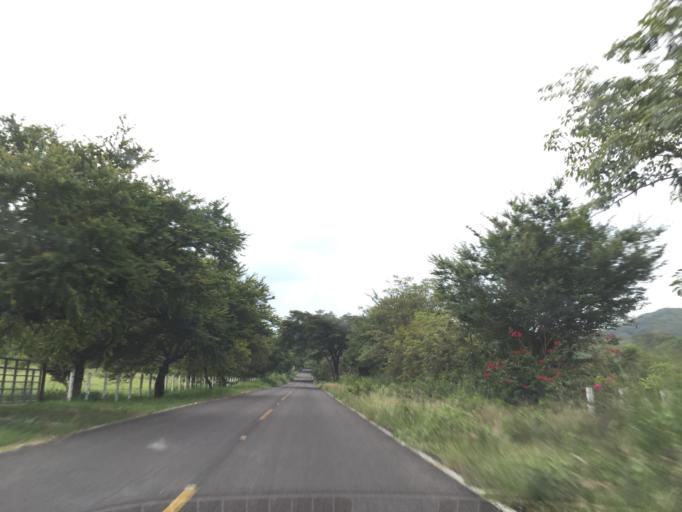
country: MX
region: Colima
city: Comala
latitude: 19.3922
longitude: -103.8022
